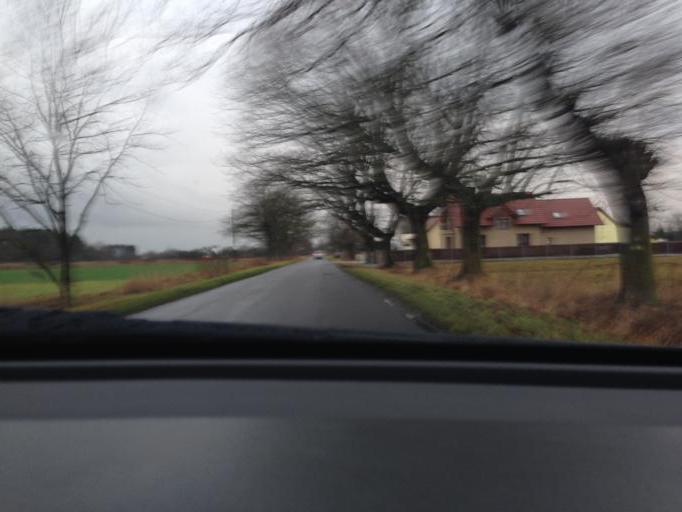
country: PL
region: Opole Voivodeship
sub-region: Powiat opolski
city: Wegry
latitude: 50.7298
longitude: 18.0644
